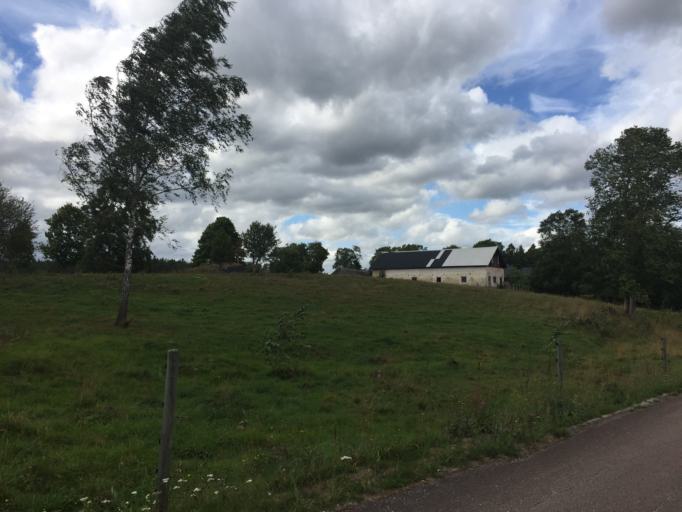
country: SE
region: OErebro
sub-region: Hallefors Kommun
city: Haellefors
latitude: 59.7864
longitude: 14.3644
